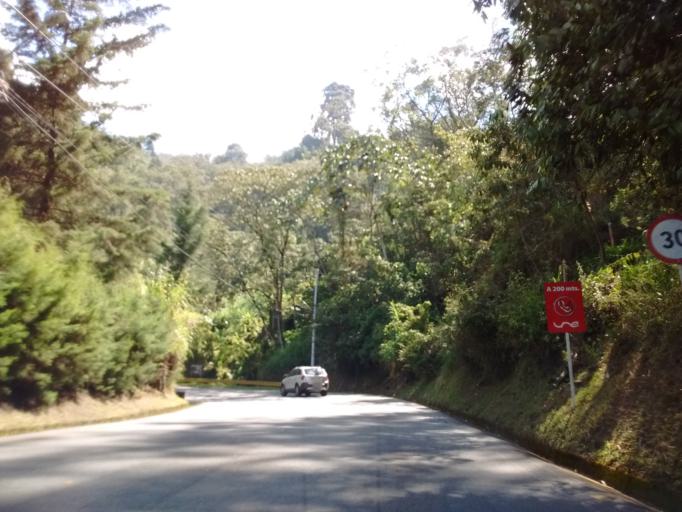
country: CO
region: Antioquia
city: Medellin
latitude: 6.2418
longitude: -75.5168
